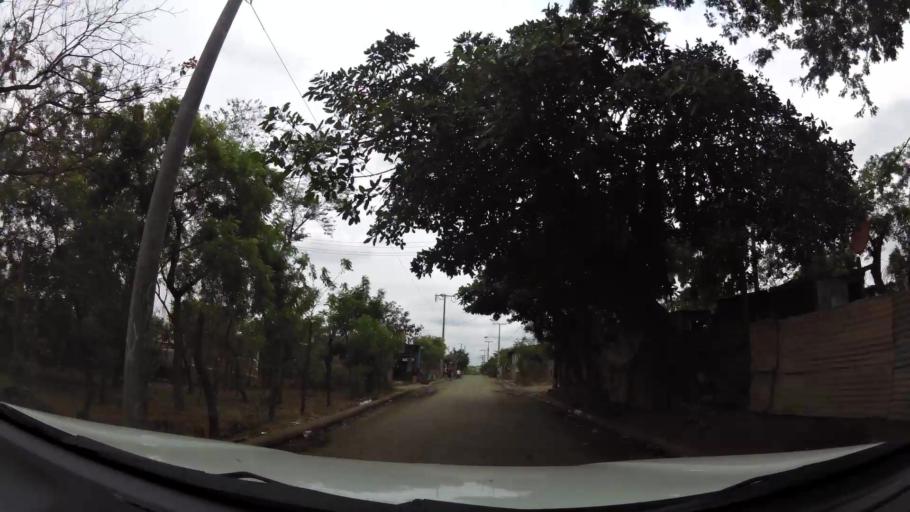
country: NI
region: Managua
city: Managua
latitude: 12.1115
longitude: -86.2190
